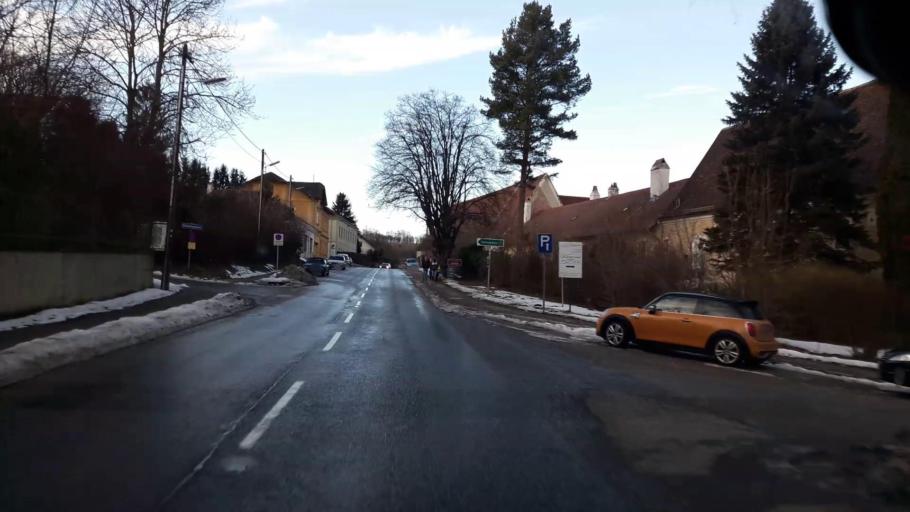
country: AT
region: Lower Austria
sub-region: Politischer Bezirk Wien-Umgebung
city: Mauerbach
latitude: 48.2493
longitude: 16.1667
